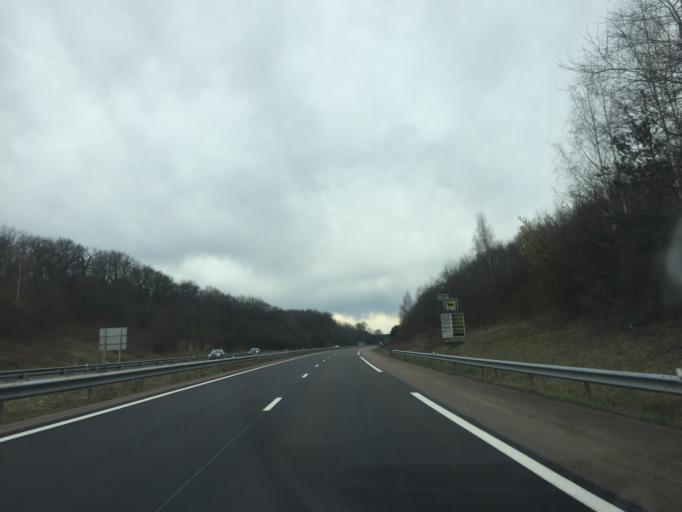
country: FR
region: Franche-Comte
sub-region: Departement du Jura
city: Bletterans
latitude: 46.7866
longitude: 5.5281
